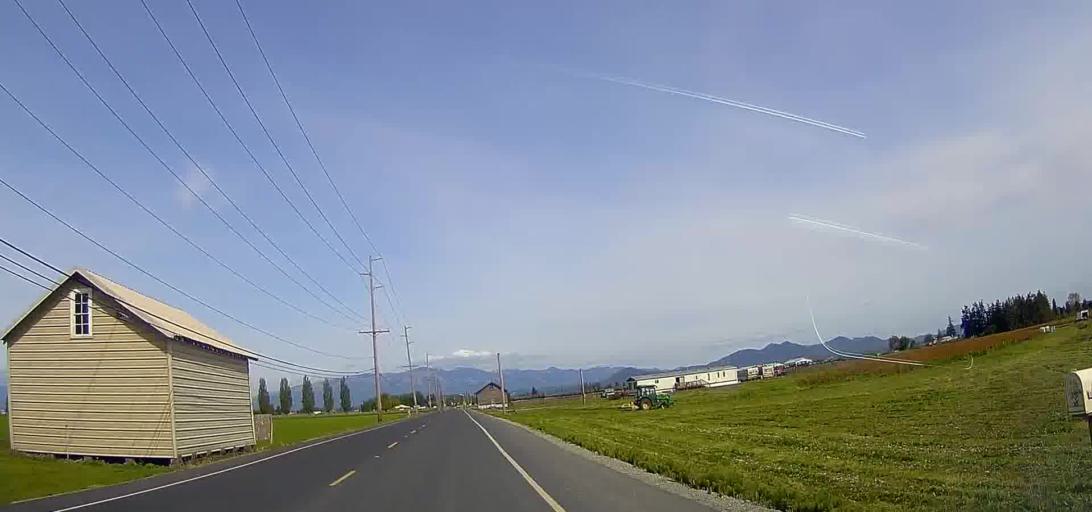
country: US
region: Washington
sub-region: Skagit County
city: Mount Vernon
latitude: 48.4207
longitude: -122.4523
